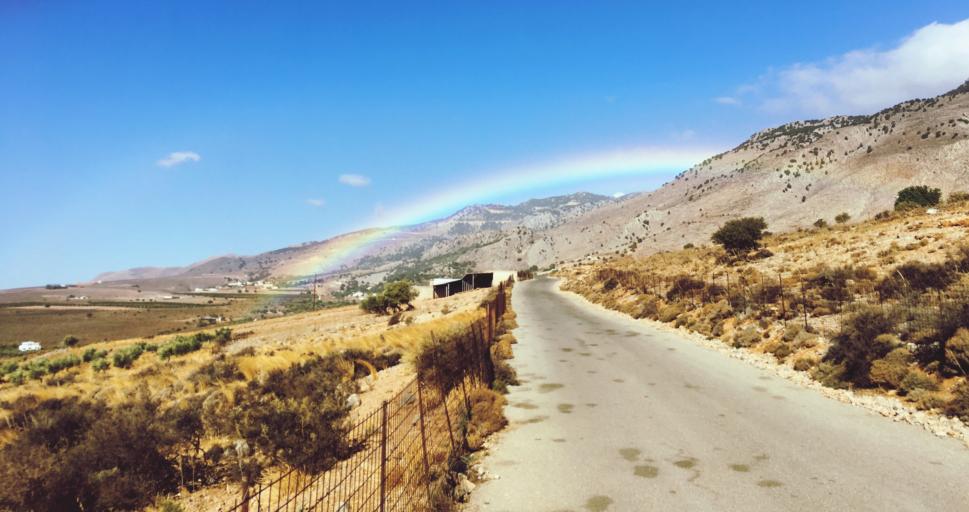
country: GR
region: Crete
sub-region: Nomos Chanias
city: Chora Sfakion
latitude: 35.2033
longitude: 24.1968
